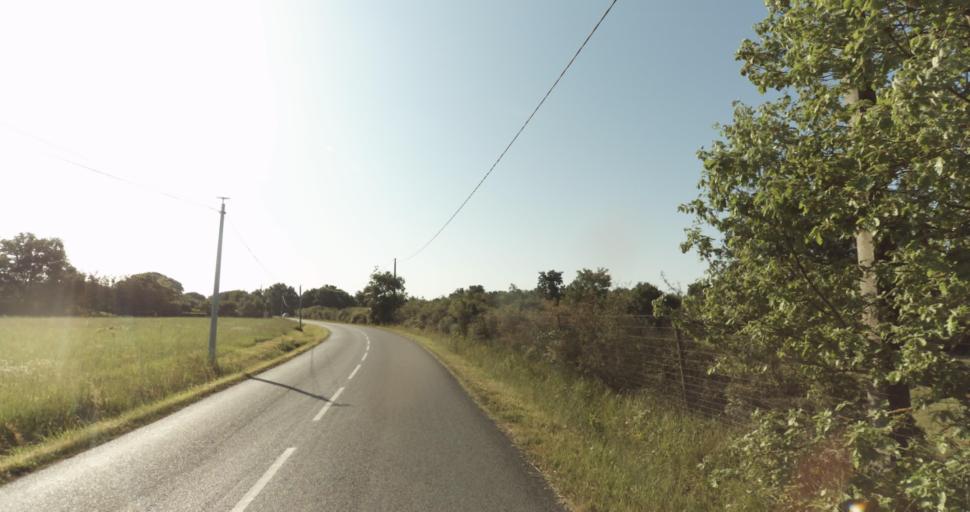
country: FR
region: Midi-Pyrenees
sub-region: Departement de la Haute-Garonne
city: Leguevin
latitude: 43.5759
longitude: 1.2304
